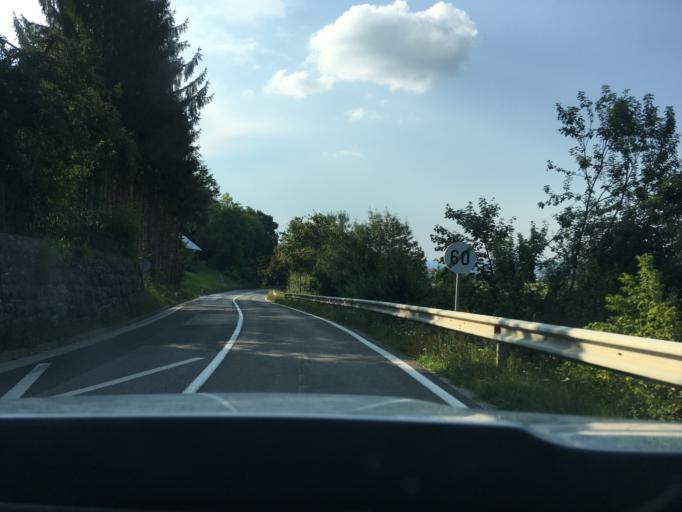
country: SI
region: Novo Mesto
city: Novo Mesto
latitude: 45.7760
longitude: 15.1861
